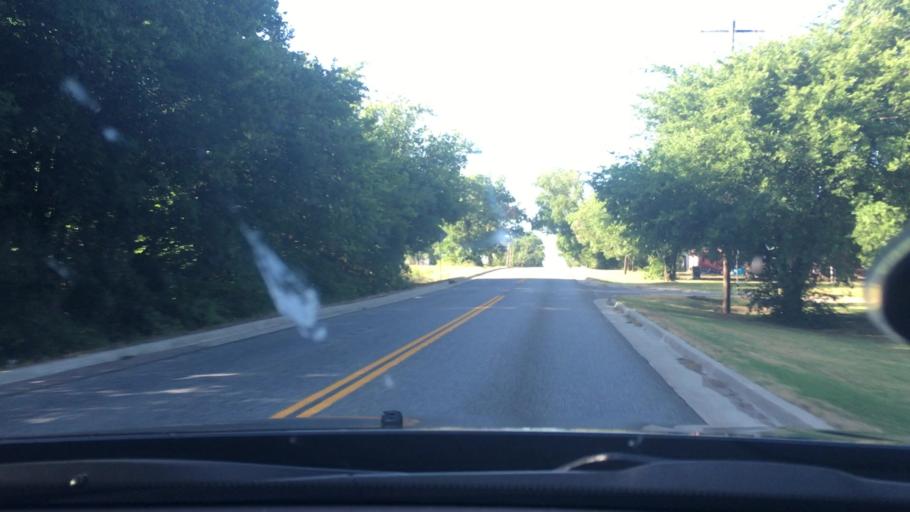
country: US
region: Oklahoma
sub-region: Murray County
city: Sulphur
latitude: 34.4025
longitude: -96.8271
